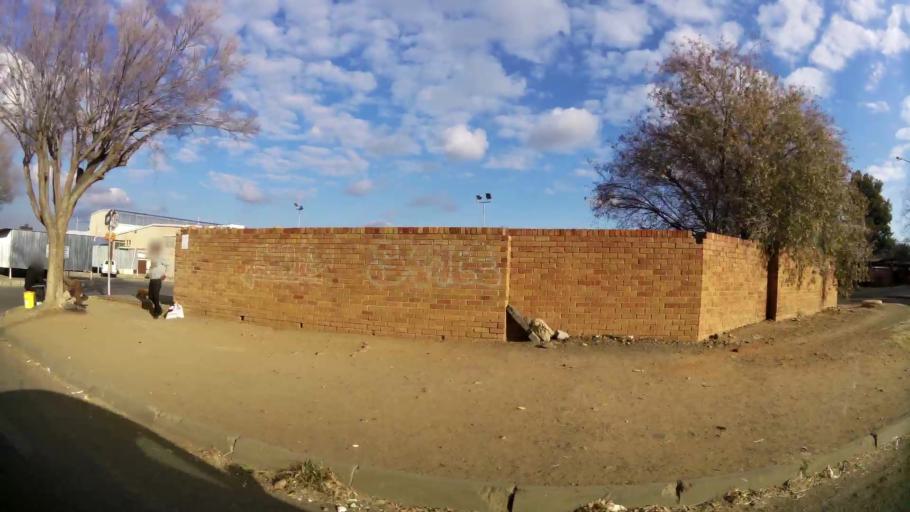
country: ZA
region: Orange Free State
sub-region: Mangaung Metropolitan Municipality
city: Bloemfontein
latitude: -29.1061
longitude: 26.1983
